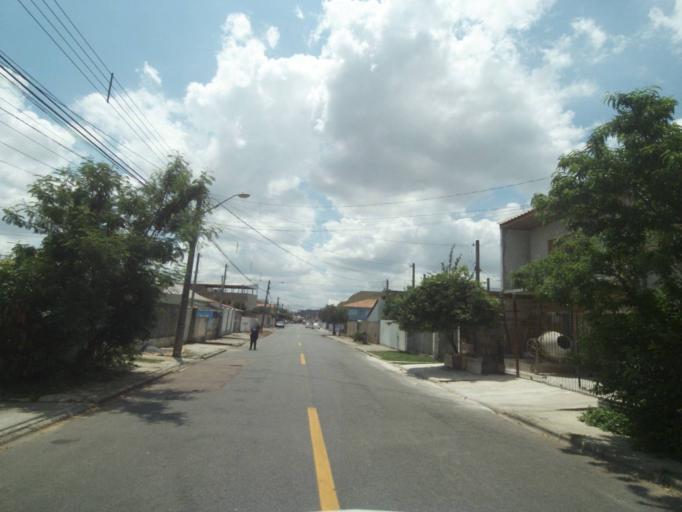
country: BR
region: Parana
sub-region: Sao Jose Dos Pinhais
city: Sao Jose dos Pinhais
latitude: -25.5396
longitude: -49.2641
